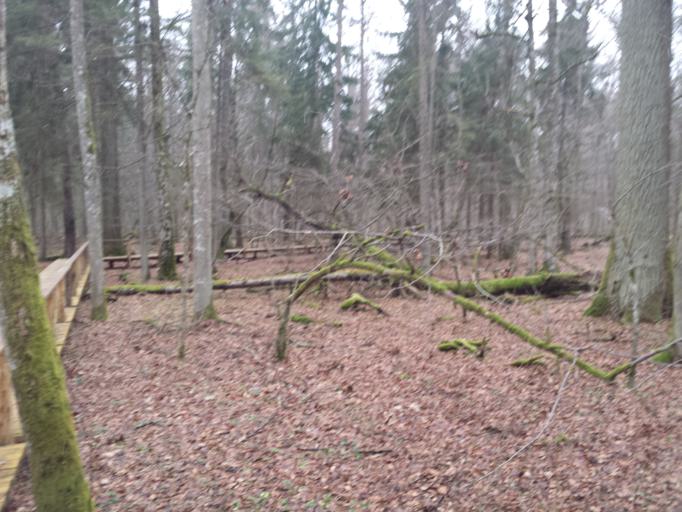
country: PL
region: Podlasie
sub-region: Powiat hajnowski
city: Bialowieza
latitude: 52.7208
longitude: 23.8405
